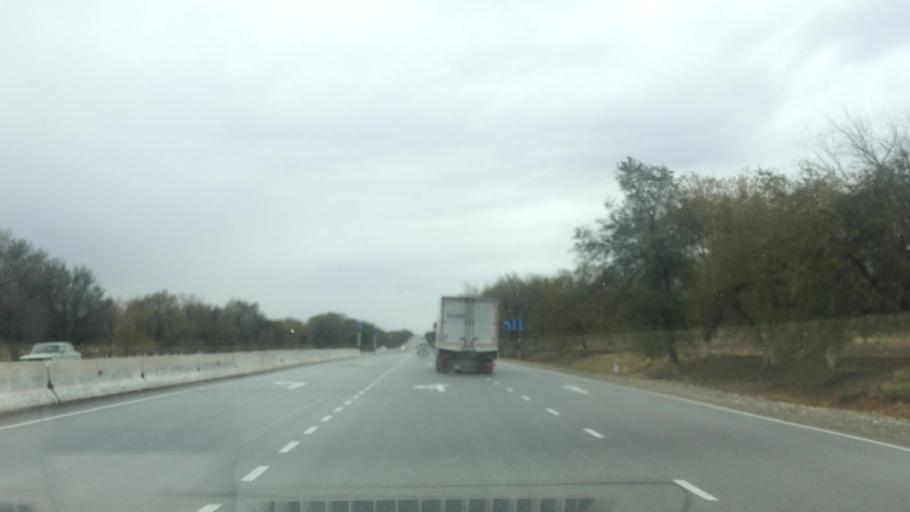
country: UZ
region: Samarqand
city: Bulung'ur
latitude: 39.9004
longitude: 67.5010
